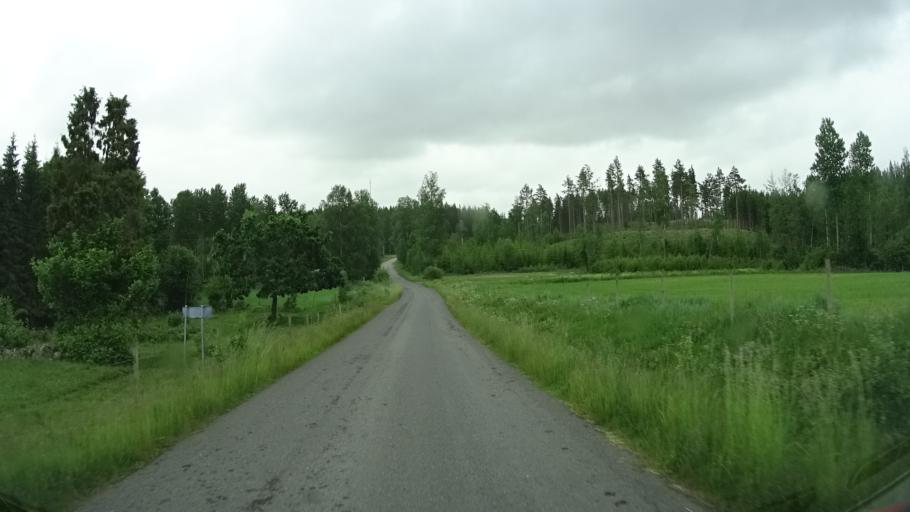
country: SE
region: Joenkoeping
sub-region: Eksjo Kommun
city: Mariannelund
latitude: 57.6902
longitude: 15.5598
